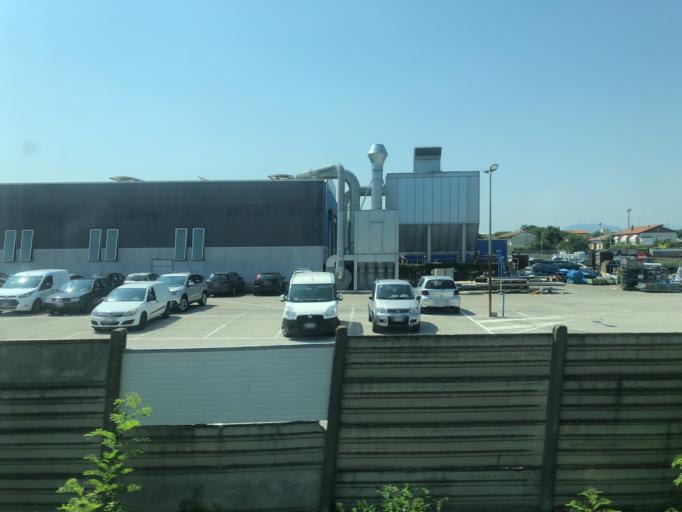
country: IT
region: Emilia-Romagna
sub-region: Provincia di Rimini
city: Rimini
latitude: 44.0708
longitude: 12.5368
